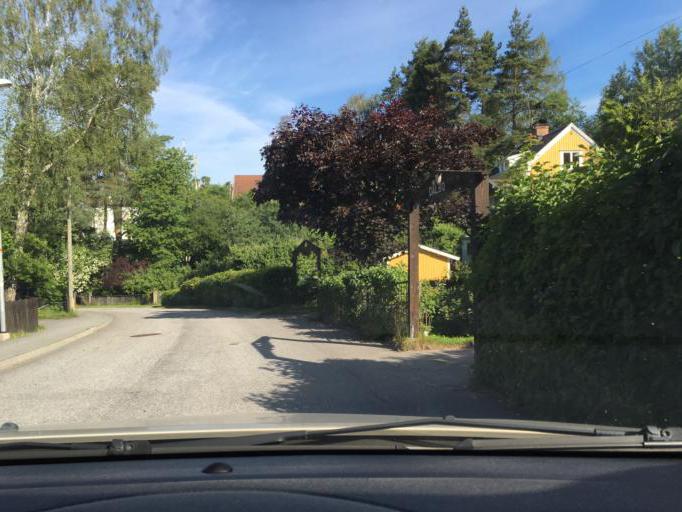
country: SE
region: Stockholm
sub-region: Sodertalje Kommun
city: Pershagen
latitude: 59.1848
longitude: 17.6582
